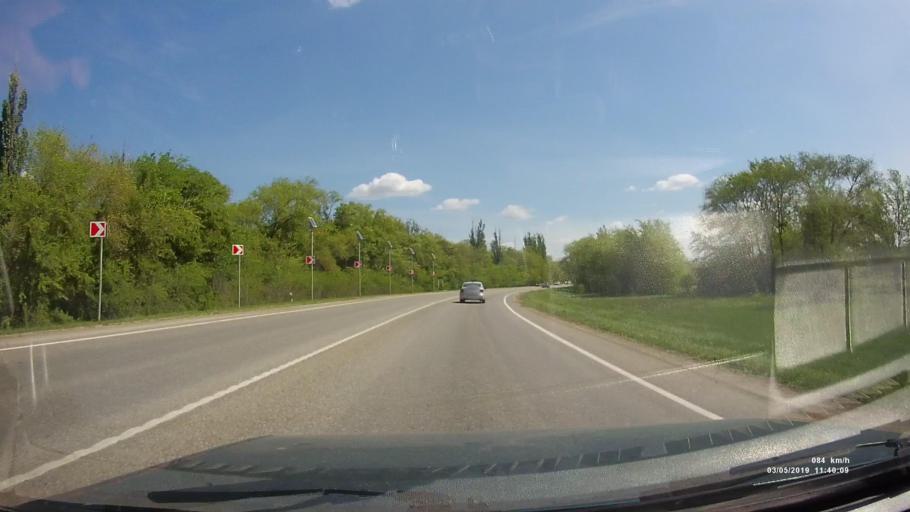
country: RU
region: Rostov
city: Ol'ginskaya
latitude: 47.1410
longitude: 39.9982
